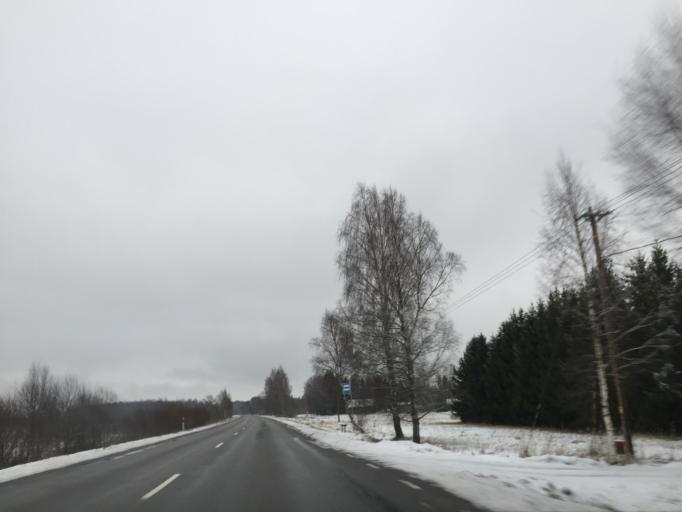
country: EE
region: Laeaene
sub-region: Lihula vald
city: Lihula
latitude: 58.6347
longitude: 23.8657
